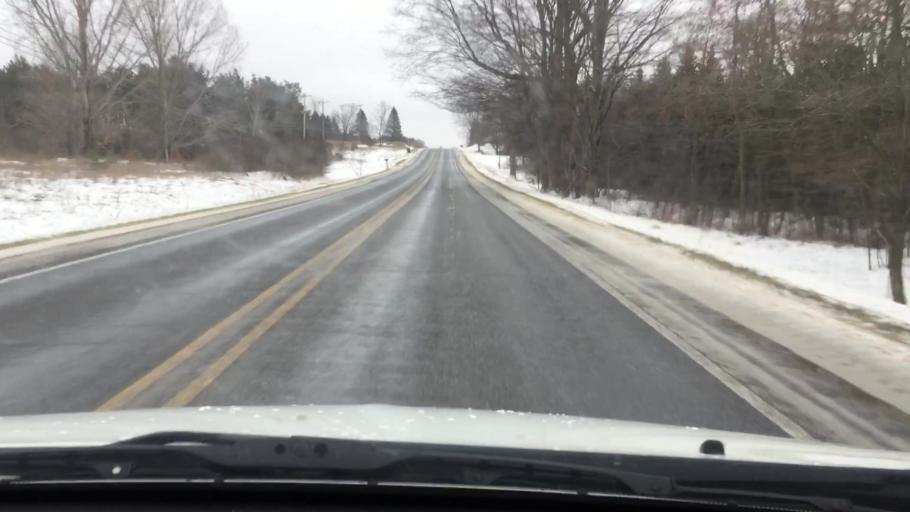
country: US
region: Michigan
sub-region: Wexford County
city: Cadillac
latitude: 44.0831
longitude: -85.4441
